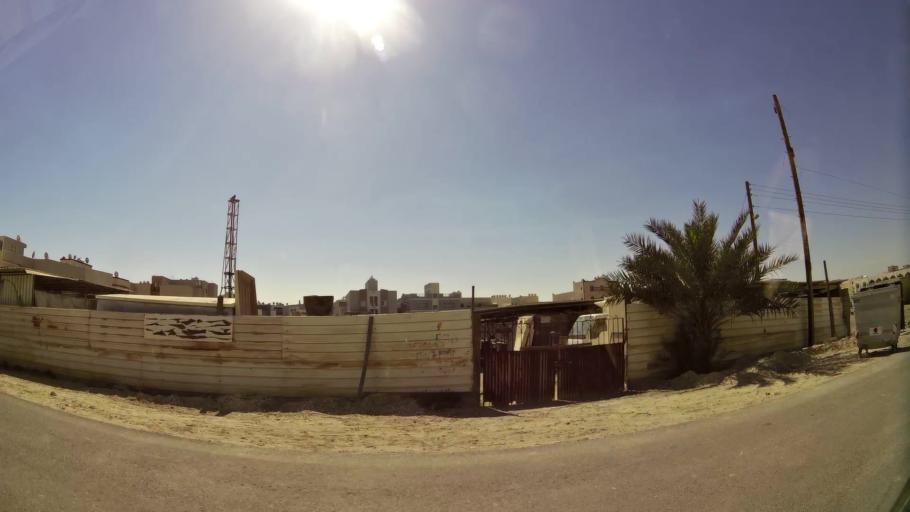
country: BH
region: Muharraq
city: Al Hadd
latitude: 26.2460
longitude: 50.6323
